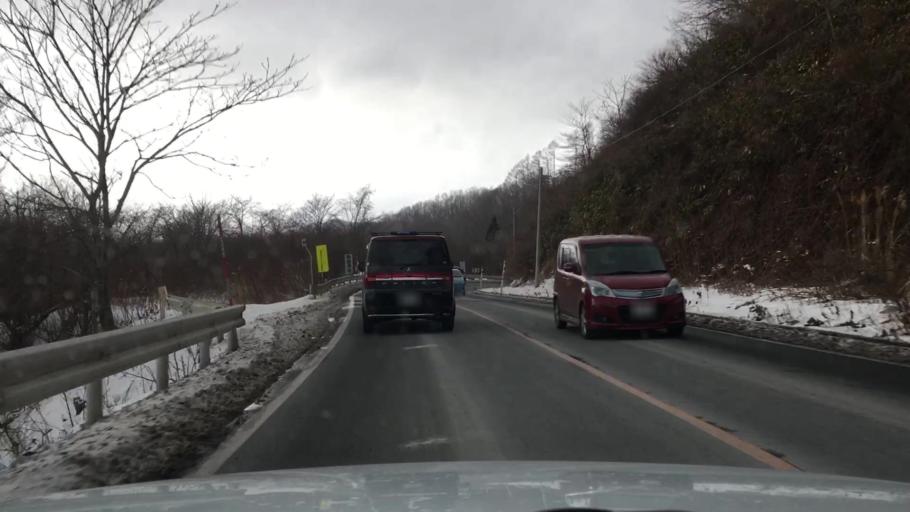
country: JP
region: Iwate
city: Morioka-shi
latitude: 39.6585
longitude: 141.3380
